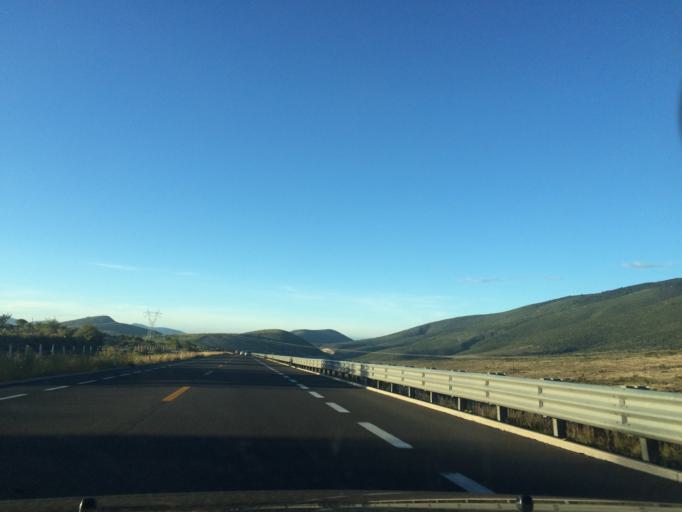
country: MX
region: Puebla
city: Morelos Canada
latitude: 18.6984
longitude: -97.4649
